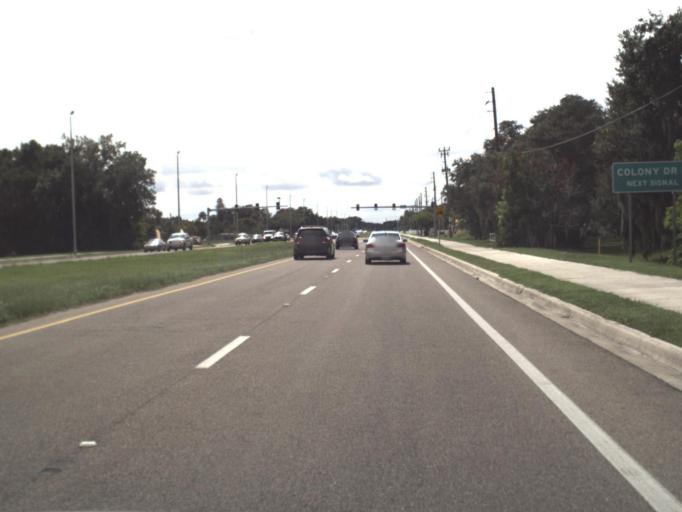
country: US
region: Florida
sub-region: Manatee County
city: Ellenton
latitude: 27.5388
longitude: -82.4854
